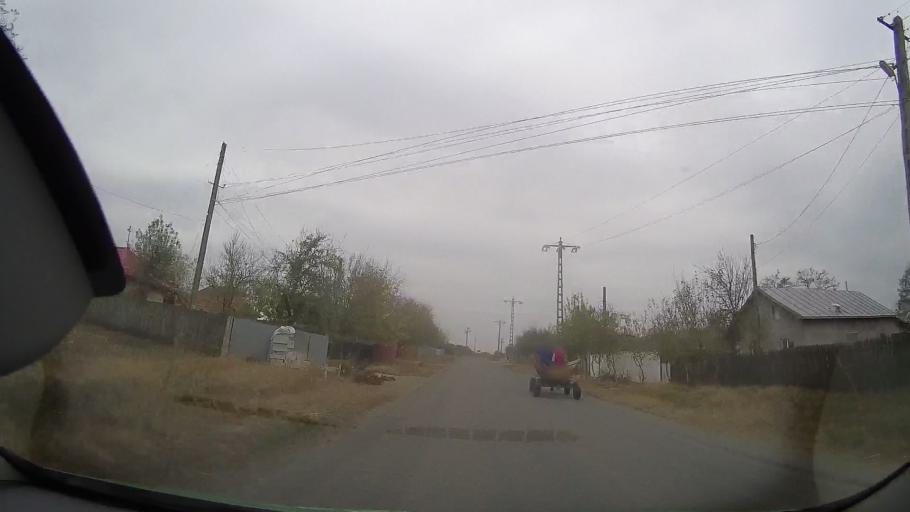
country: RO
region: Buzau
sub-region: Comuna Luciu
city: Luciu
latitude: 44.9720
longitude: 27.0304
